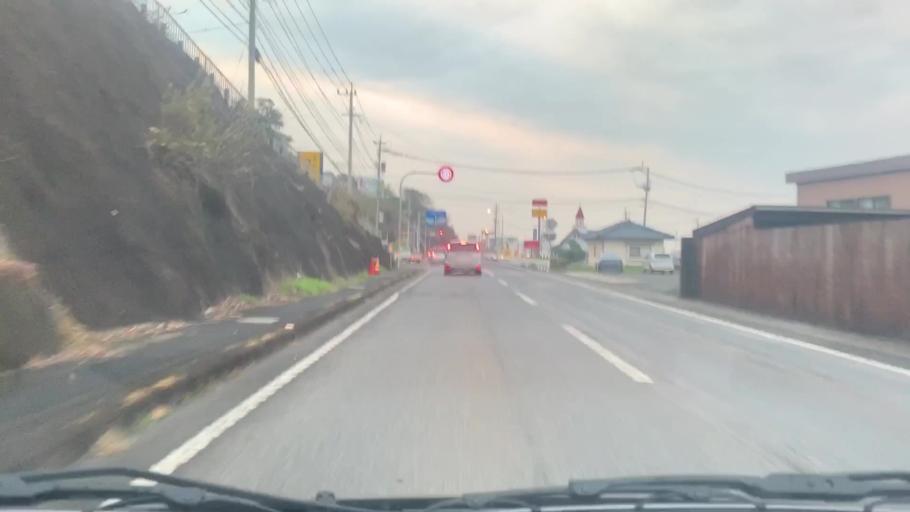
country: JP
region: Saga Prefecture
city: Ureshinomachi-shimojuku
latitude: 33.0371
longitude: 129.9224
